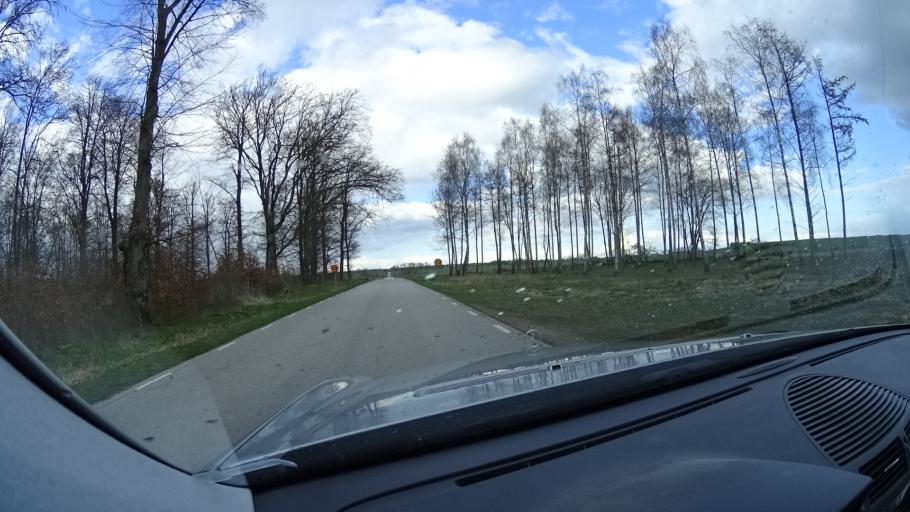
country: SE
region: Skane
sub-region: Eslovs Kommun
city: Eslov
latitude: 55.8073
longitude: 13.3746
